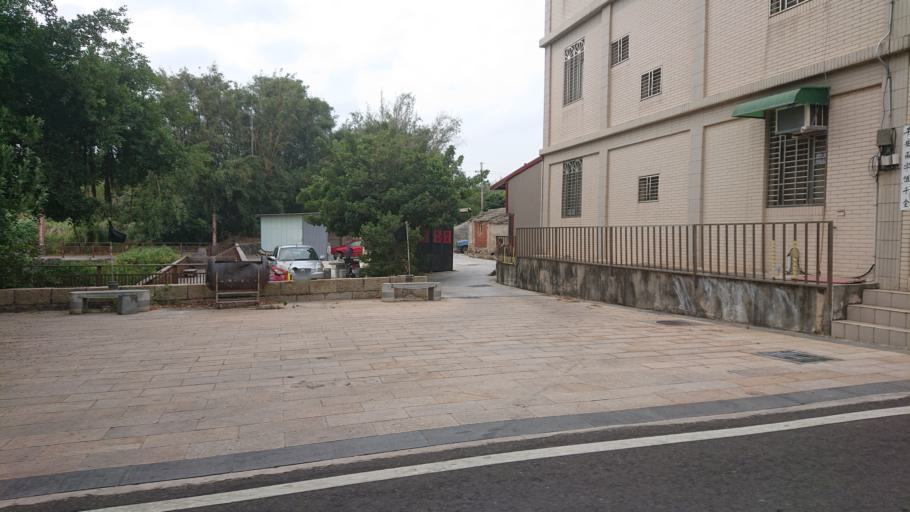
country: TW
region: Fukien
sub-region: Kinmen
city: Jincheng
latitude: 24.4163
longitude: 118.3110
